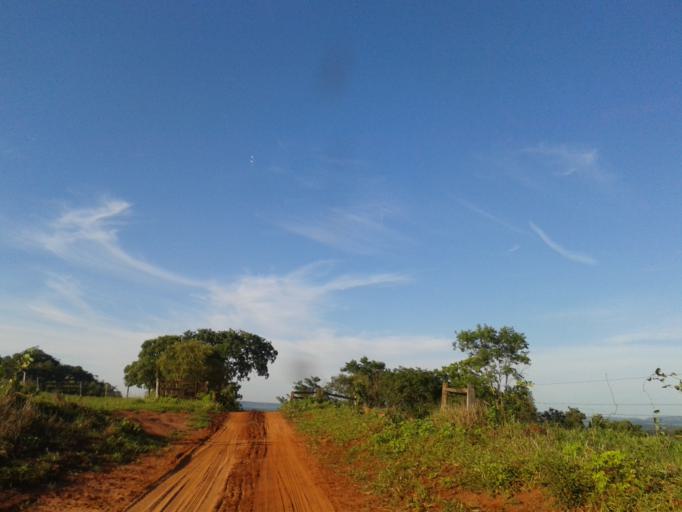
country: BR
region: Minas Gerais
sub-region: Santa Vitoria
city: Santa Vitoria
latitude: -18.9777
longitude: -49.8917
